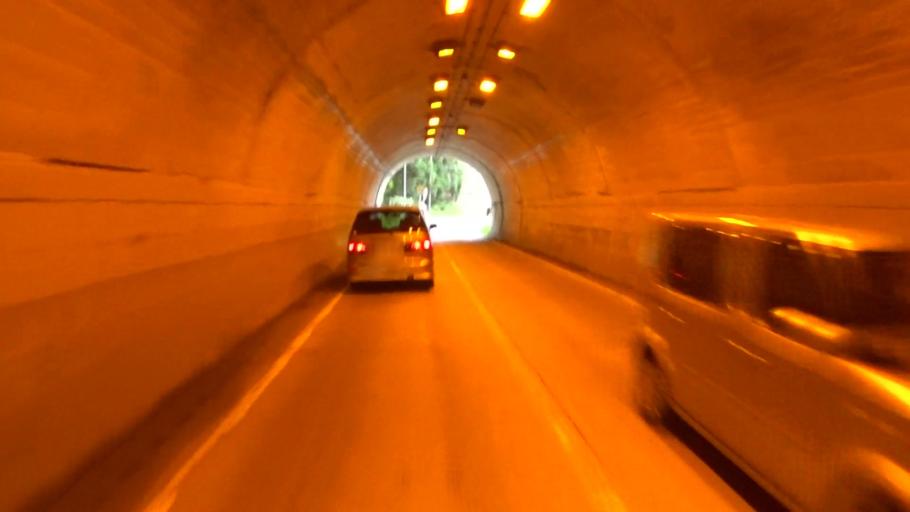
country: JP
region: Kyoto
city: Uji
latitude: 34.8607
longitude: 135.9091
